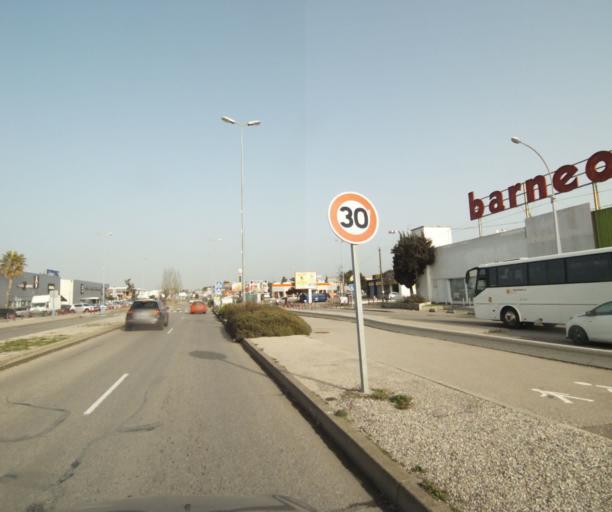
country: FR
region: Provence-Alpes-Cote d'Azur
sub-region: Departement des Bouches-du-Rhone
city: Septemes-les-Vallons
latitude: 43.4175
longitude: 5.3578
